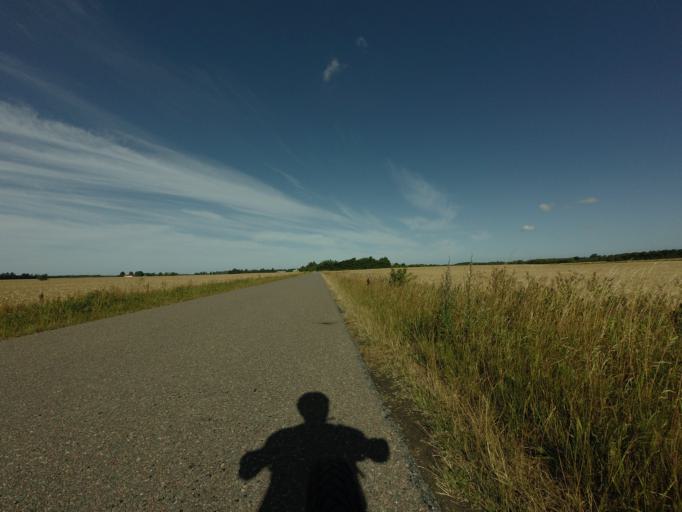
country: DK
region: North Denmark
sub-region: Hjorring Kommune
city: Vra
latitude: 57.3903
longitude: 9.9778
